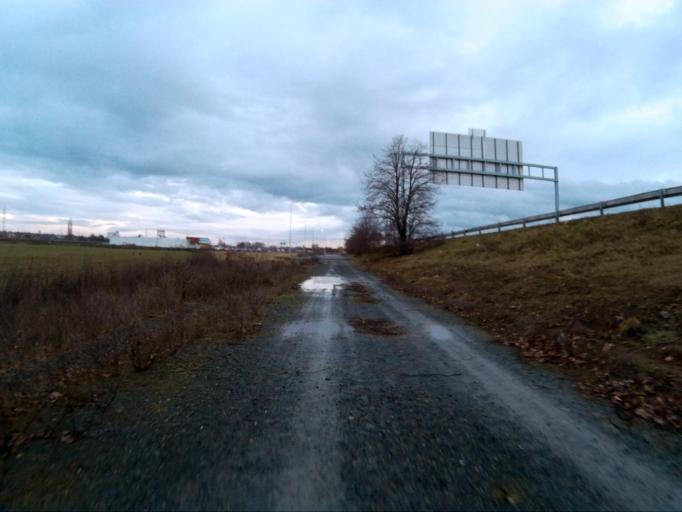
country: CZ
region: South Moravian
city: Modrice
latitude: 49.1402
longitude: 16.6352
